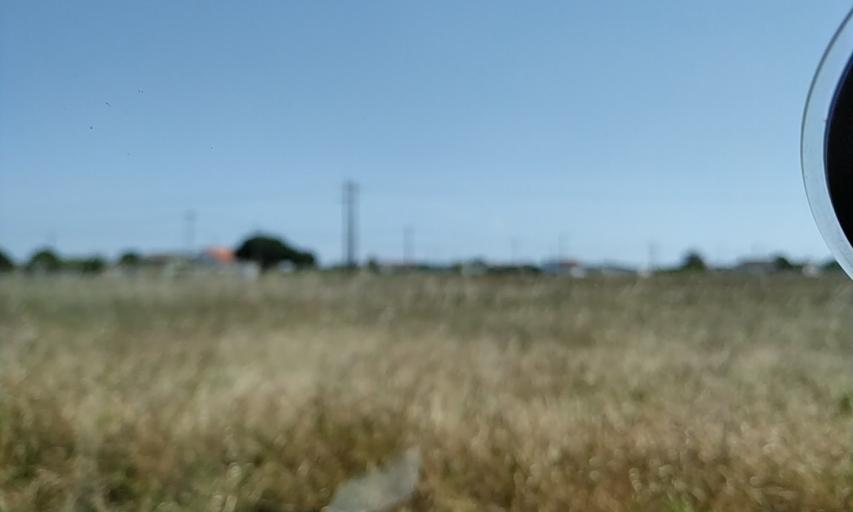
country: PT
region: Setubal
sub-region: Palmela
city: Palmela
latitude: 38.6135
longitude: -8.7626
